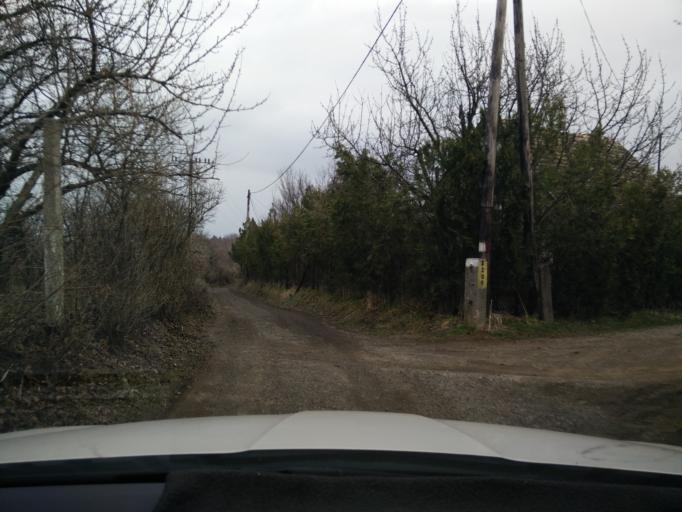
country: HU
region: Tolna
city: Szekszard
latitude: 46.3490
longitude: 18.6668
